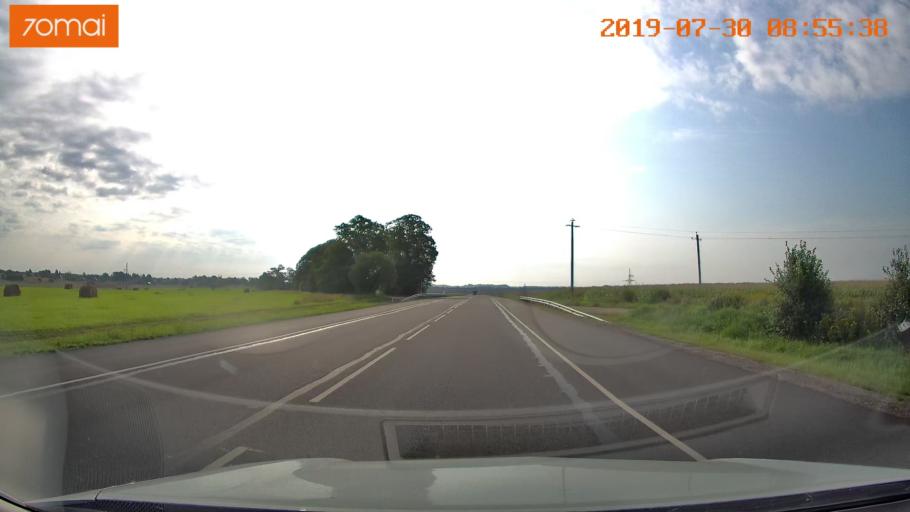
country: RU
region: Kaliningrad
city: Gusev
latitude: 54.6007
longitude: 22.0554
